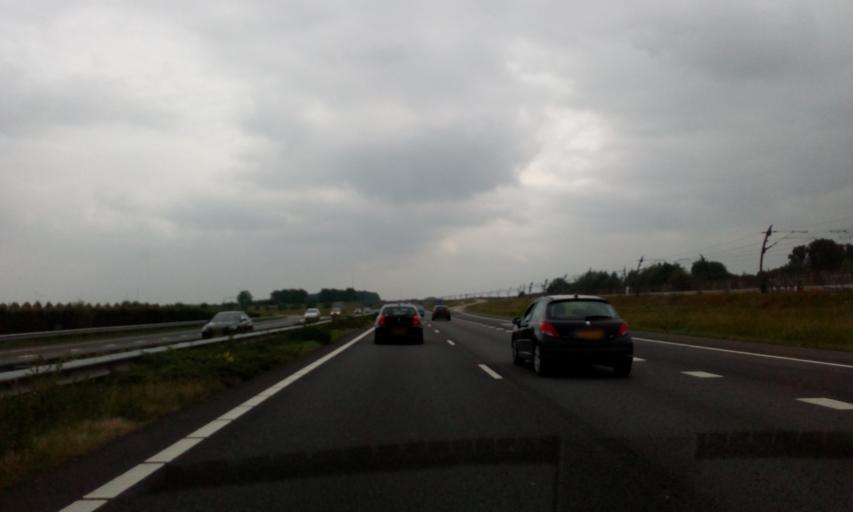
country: NL
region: Gelderland
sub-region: Gemeente Geldermalsen
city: Geldermalsen
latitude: 51.8760
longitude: 5.3499
